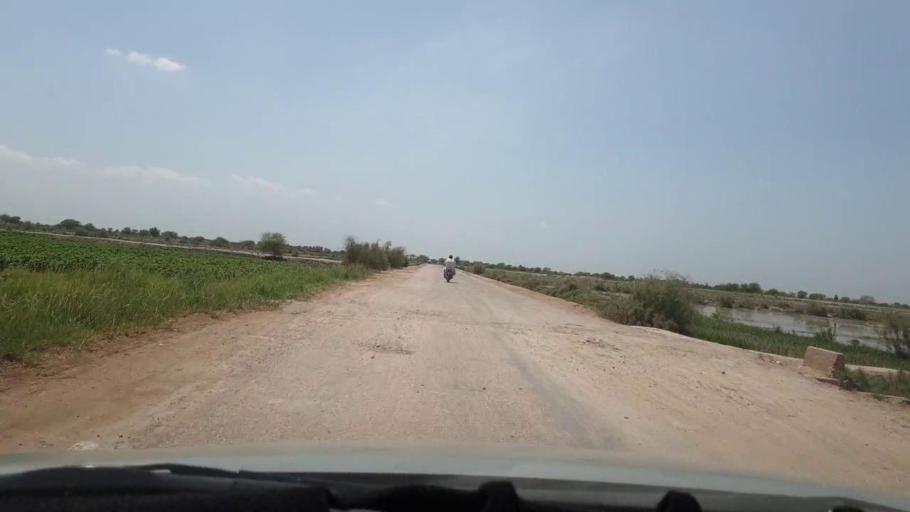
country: PK
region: Sindh
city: Pano Aqil
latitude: 27.6634
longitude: 69.1577
